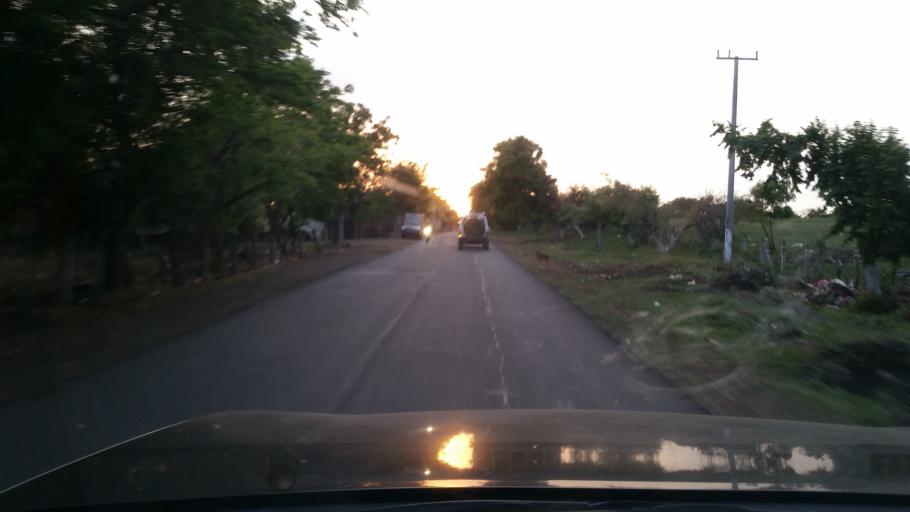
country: NI
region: Managua
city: Masachapa
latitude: 11.7777
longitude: -86.5094
